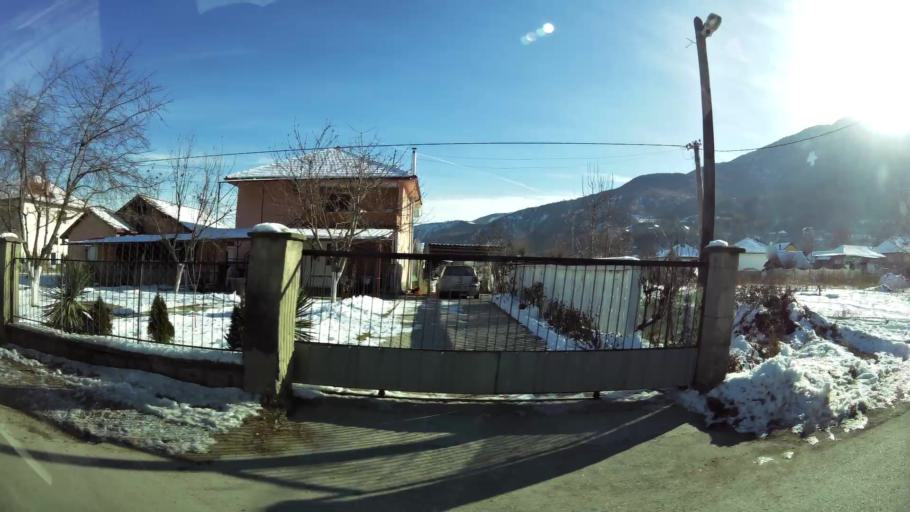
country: MK
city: Grchec
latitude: 41.9768
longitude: 21.3091
